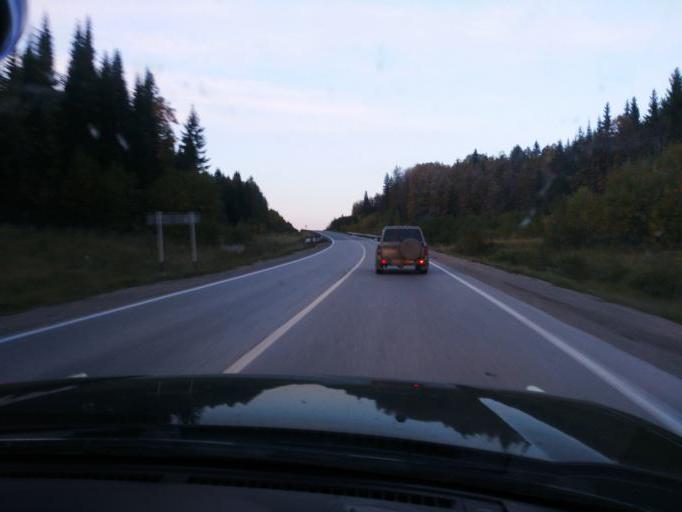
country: RU
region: Perm
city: Sylva
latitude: 58.2841
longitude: 56.7359
